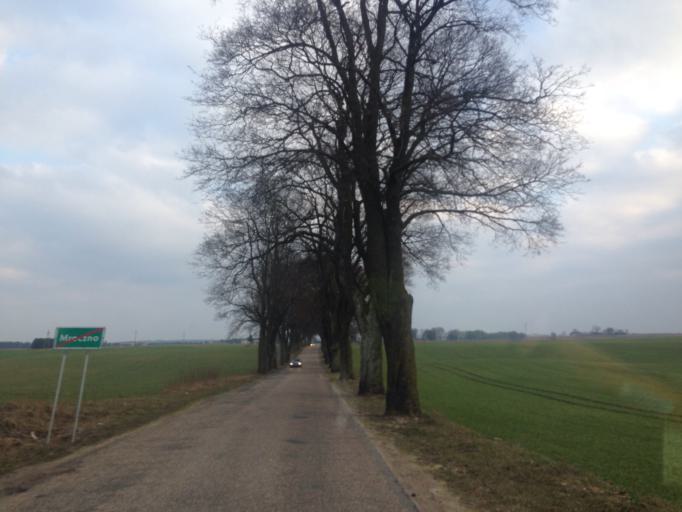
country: PL
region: Kujawsko-Pomorskie
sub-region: Powiat brodnicki
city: Brzozie
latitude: 53.3490
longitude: 19.7075
